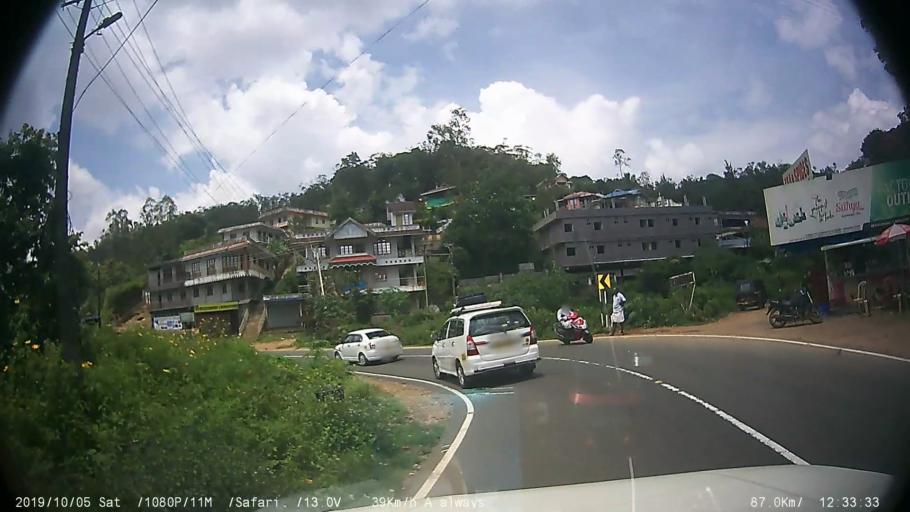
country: IN
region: Tamil Nadu
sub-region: Theni
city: Gudalur
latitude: 9.5778
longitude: 77.0205
